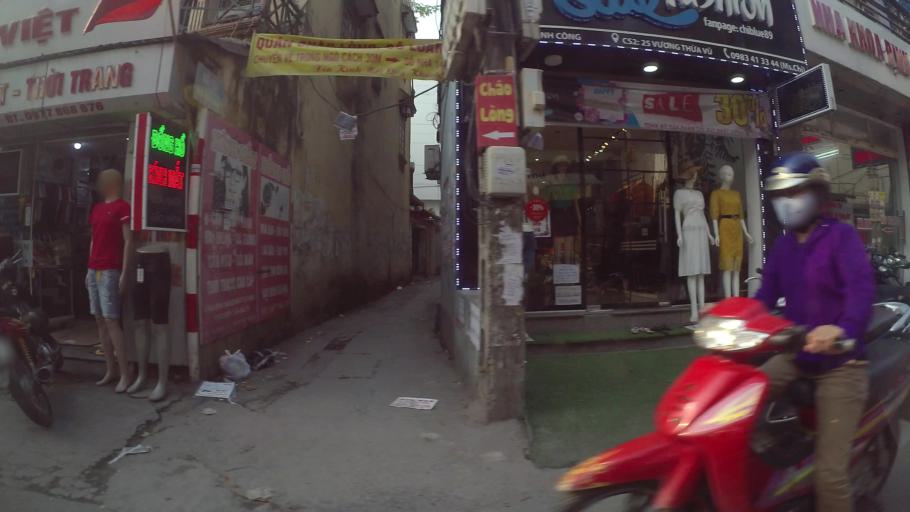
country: VN
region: Ha Noi
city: Hai BaTrung
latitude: 20.9824
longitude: 105.8332
